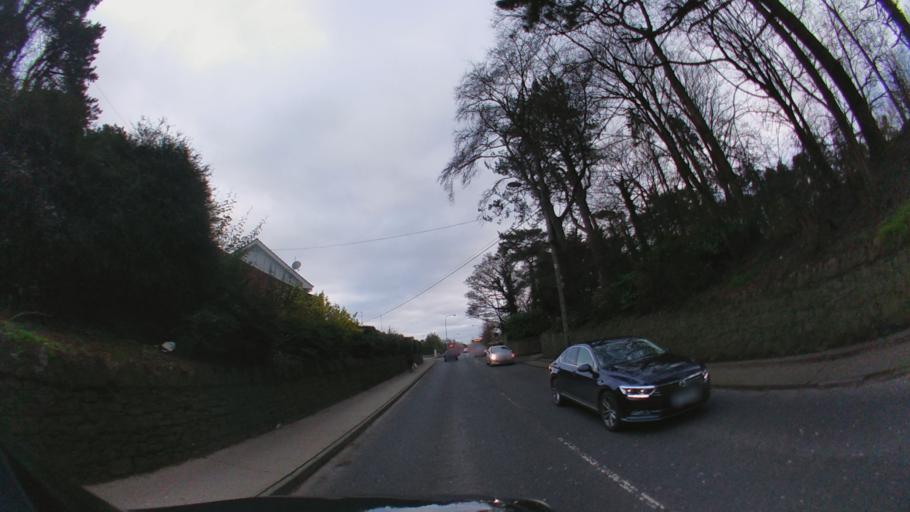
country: IE
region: Leinster
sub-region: Lu
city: Drogheda
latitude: 53.7110
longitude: -6.3356
